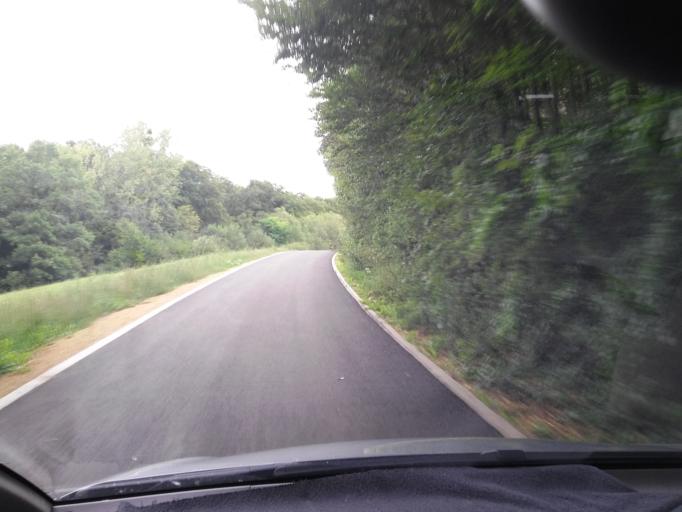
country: BE
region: Wallonia
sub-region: Province du Luxembourg
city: Attert
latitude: 49.7354
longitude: 5.8052
